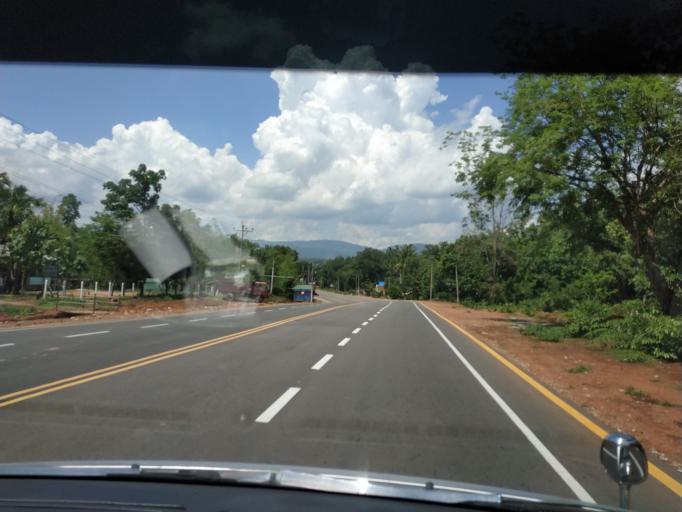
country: MM
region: Mon
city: Kyaikto
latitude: 17.3628
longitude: 97.0457
